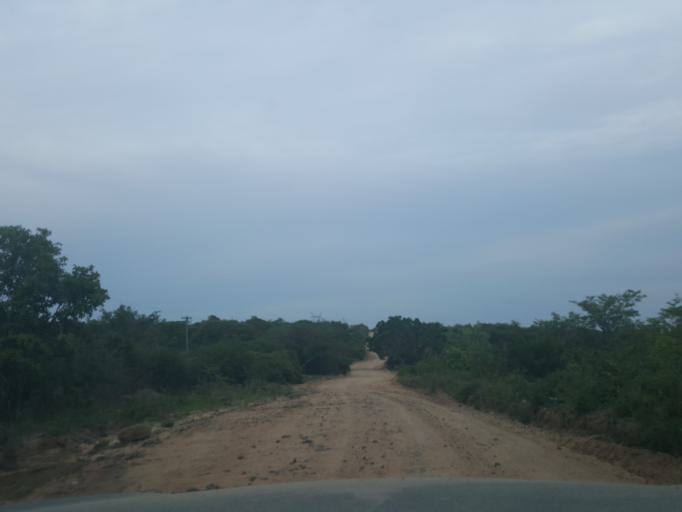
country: ZA
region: Limpopo
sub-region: Mopani District Municipality
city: Hoedspruit
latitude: -24.5545
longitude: 31.0233
